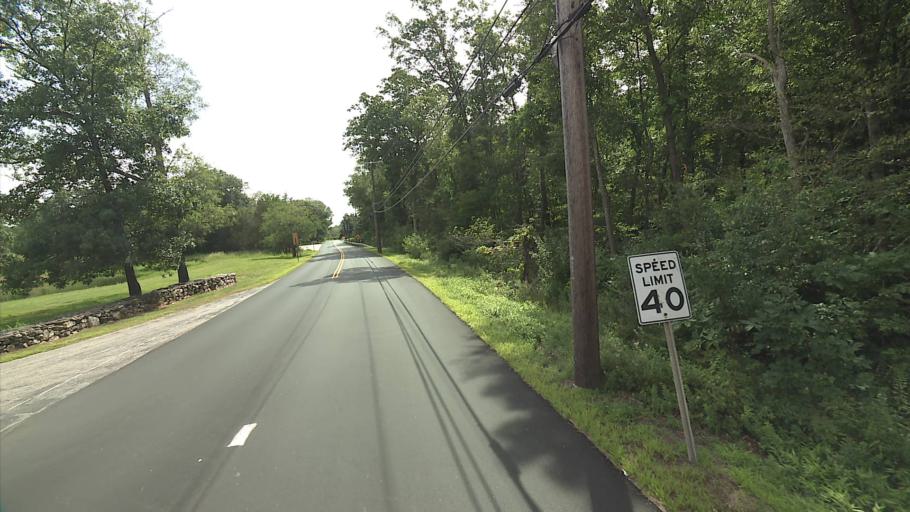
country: US
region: Connecticut
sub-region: Windham County
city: South Woodstock
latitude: 41.9374
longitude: -71.9849
